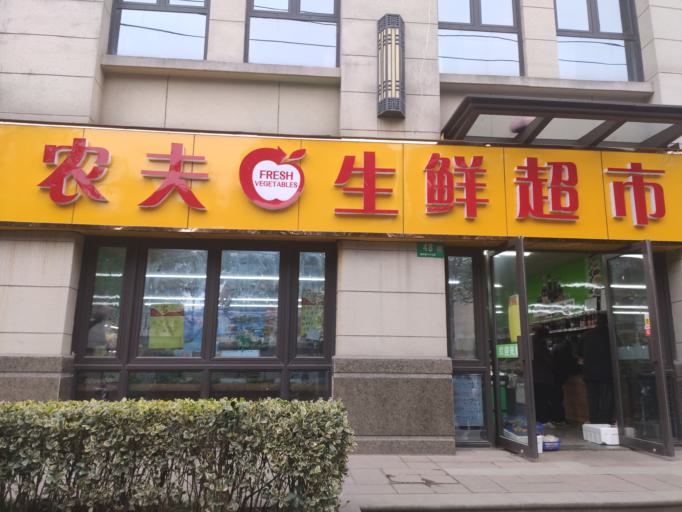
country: CN
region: Shanghai Shi
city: Huacao
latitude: 31.2094
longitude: 121.2872
